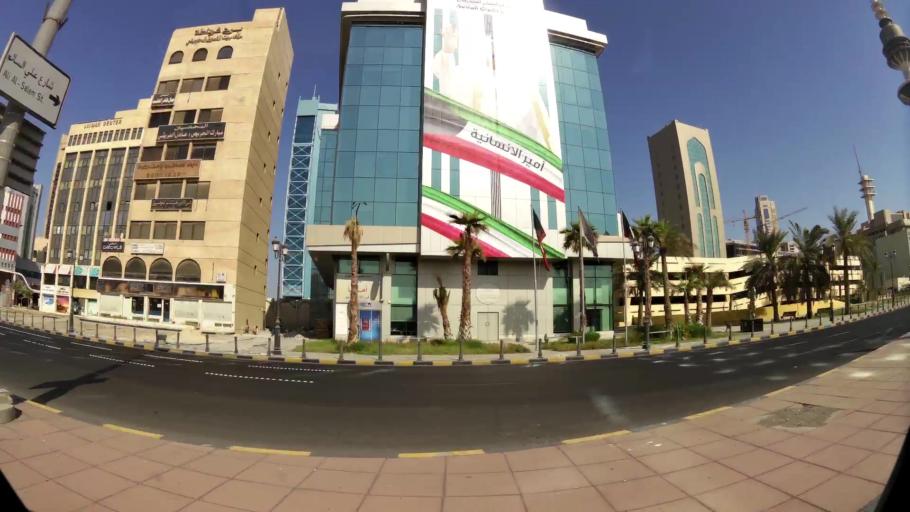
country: KW
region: Al Asimah
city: Kuwait City
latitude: 29.3662
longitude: 47.9716
